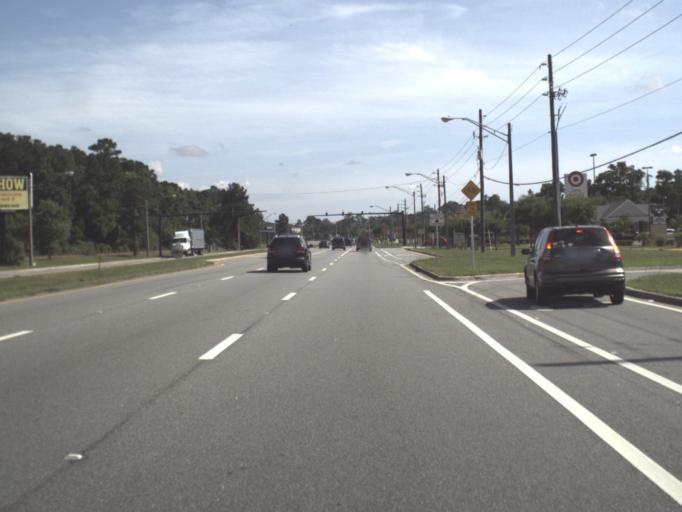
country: US
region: Florida
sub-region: Clay County
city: Orange Park
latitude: 30.2342
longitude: -81.6979
